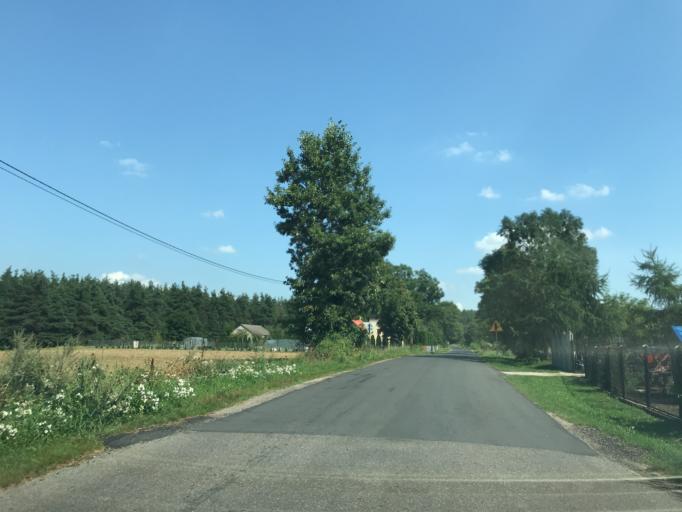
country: PL
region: Masovian Voivodeship
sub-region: Powiat zurominski
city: Lubowidz
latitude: 53.1750
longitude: 19.8586
